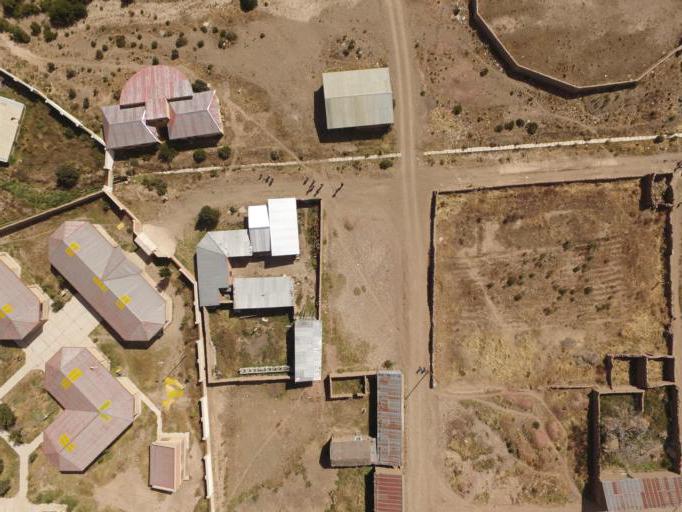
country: BO
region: Oruro
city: Challapata
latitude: -18.6926
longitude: -66.7577
